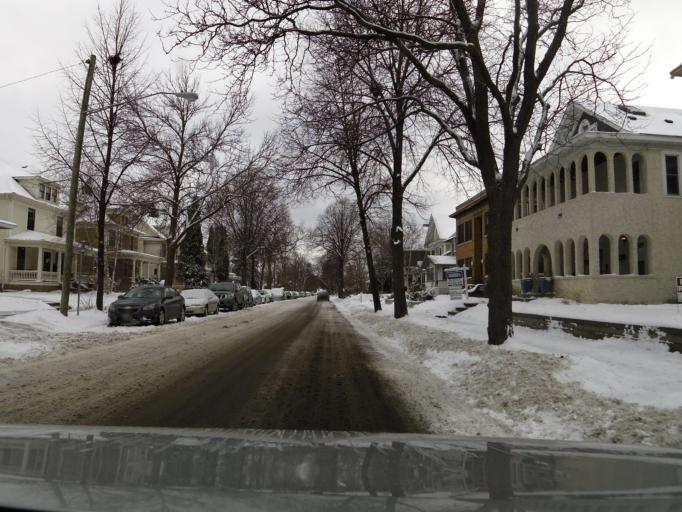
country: US
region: Minnesota
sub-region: Hennepin County
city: Saint Louis Park
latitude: 44.9462
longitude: -93.3009
